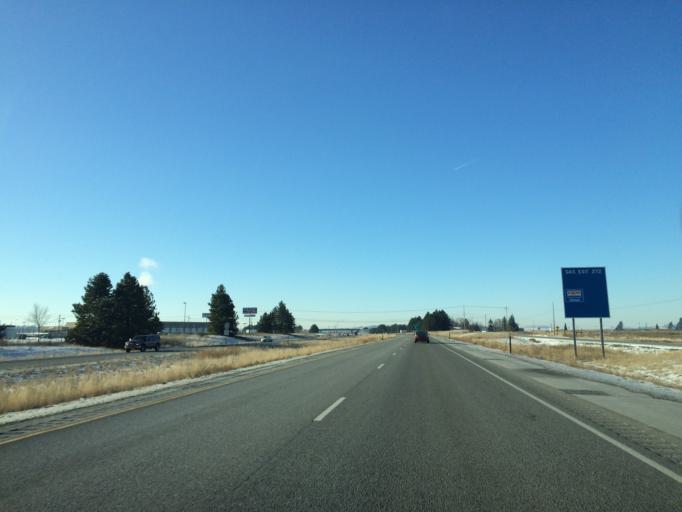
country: US
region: Washington
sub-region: Spokane County
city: Airway Heights
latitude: 47.5970
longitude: -117.5562
